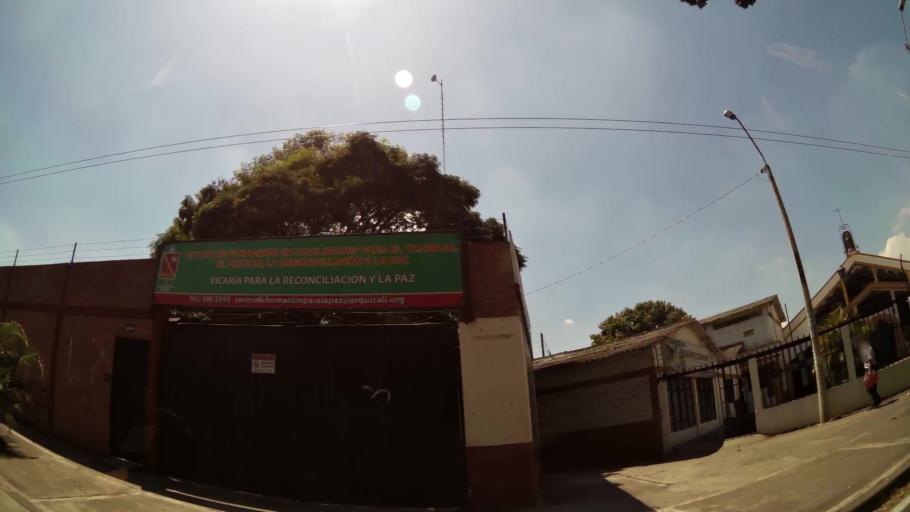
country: CO
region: Valle del Cauca
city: Cali
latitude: 3.4372
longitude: -76.4972
